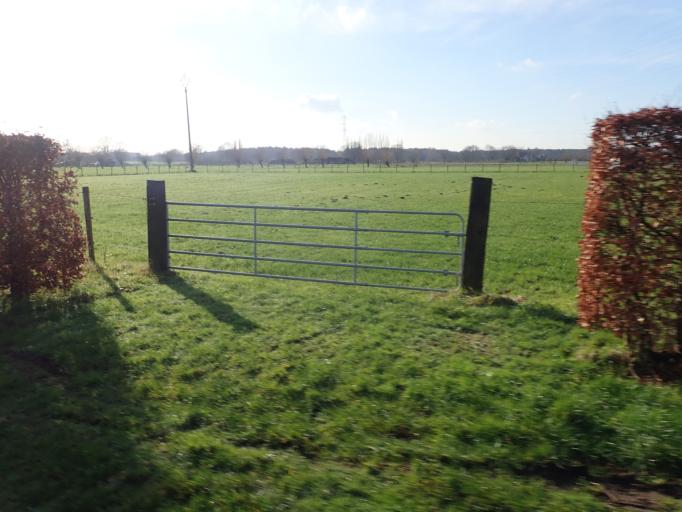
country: BE
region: Flanders
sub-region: Provincie Antwerpen
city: Putte
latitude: 51.0389
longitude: 4.6282
